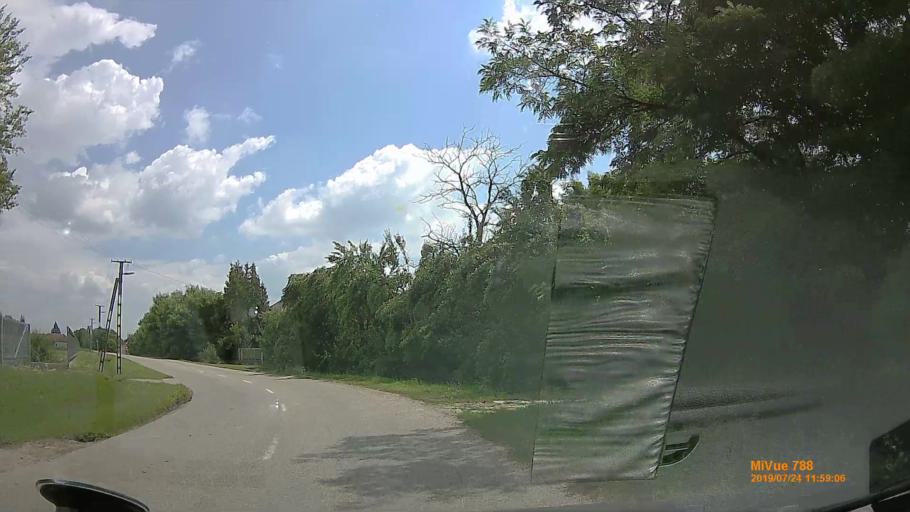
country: HU
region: Szabolcs-Szatmar-Bereg
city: Tarpa
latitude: 48.2023
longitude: 22.4483
